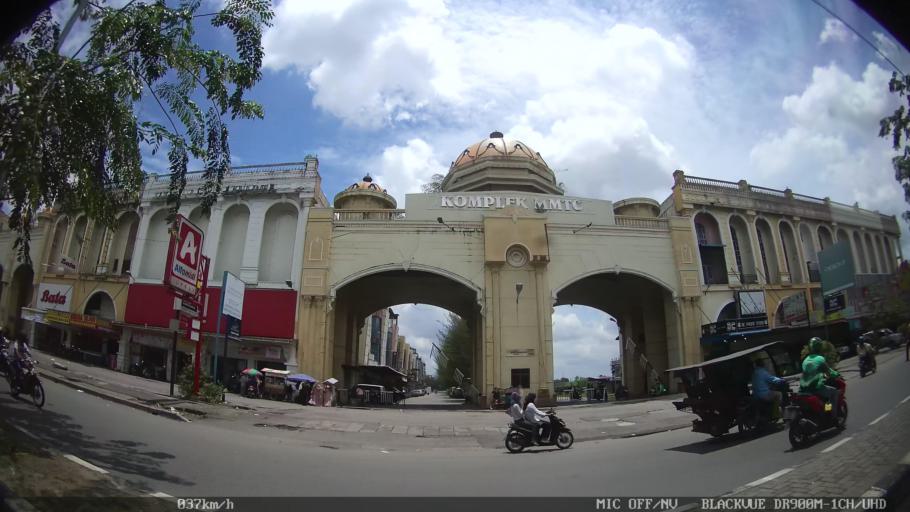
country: ID
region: North Sumatra
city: Medan
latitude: 3.6028
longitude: 98.7068
